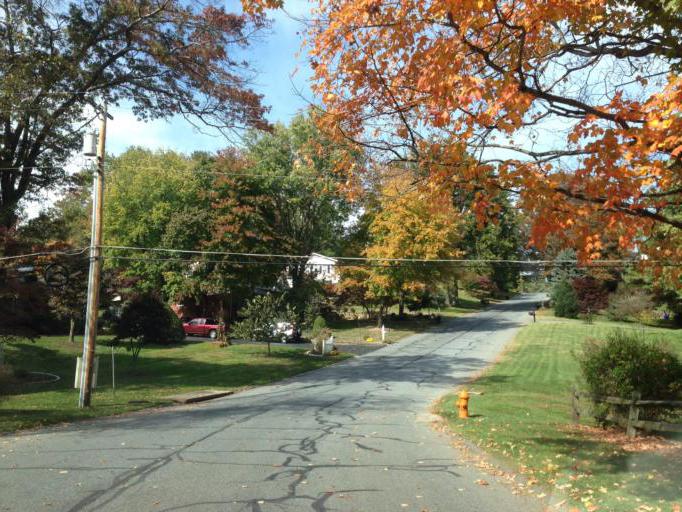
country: US
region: Maryland
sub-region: Howard County
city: Columbia
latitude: 39.2833
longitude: -76.8486
